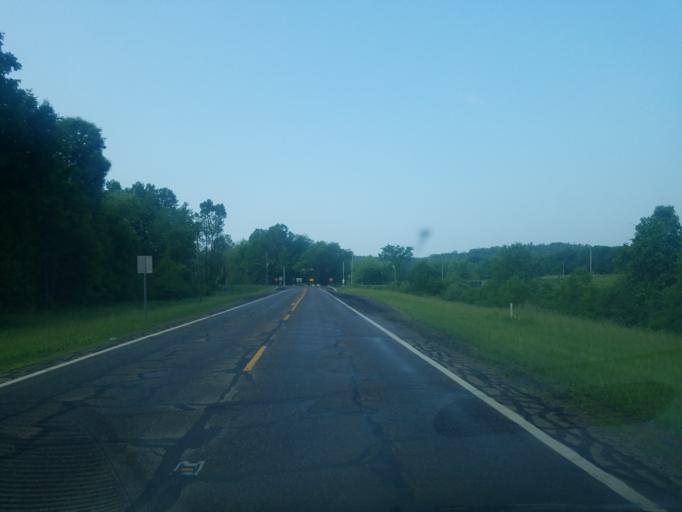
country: US
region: Ohio
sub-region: Tuscarawas County
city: Rockford
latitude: 40.5139
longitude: -81.2629
